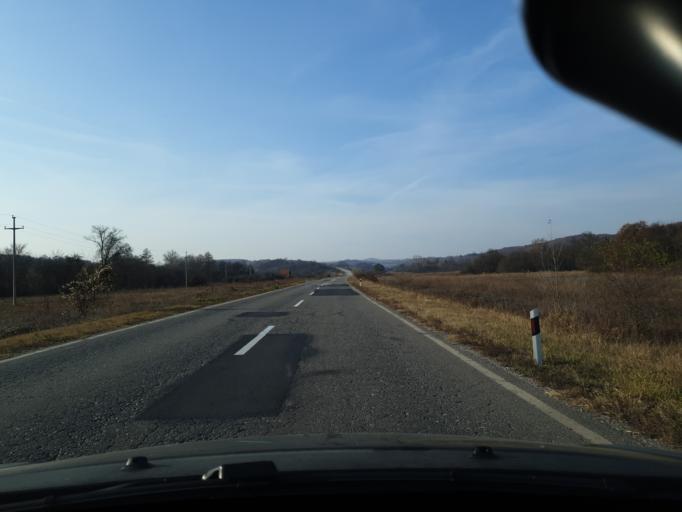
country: RS
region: Central Serbia
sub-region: Zajecarski Okrug
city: Zajecar
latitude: 43.9519
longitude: 22.2835
